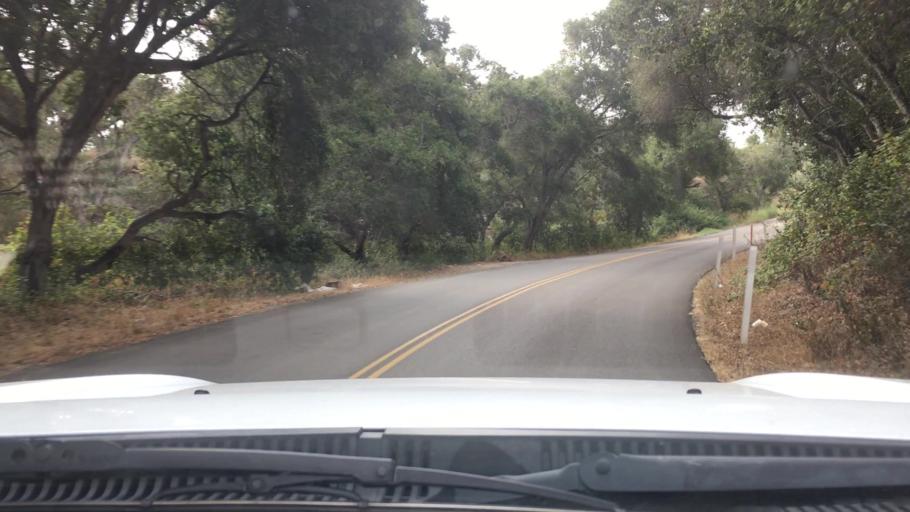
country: US
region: California
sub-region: San Luis Obispo County
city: Arroyo Grande
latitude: 35.1099
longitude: -120.5631
